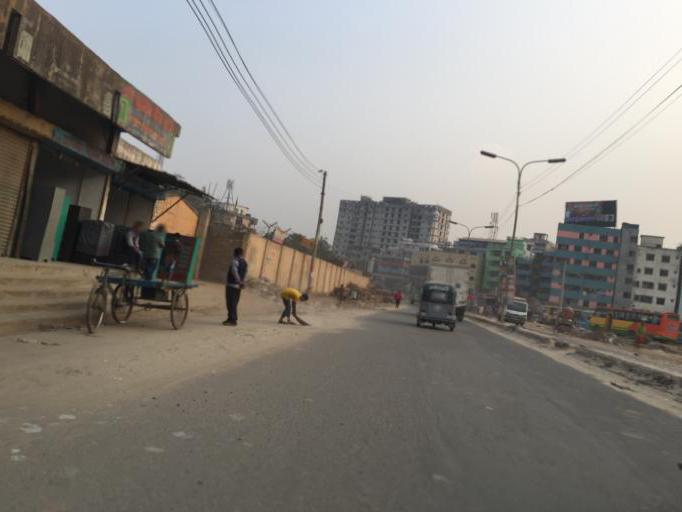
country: BD
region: Dhaka
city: Azimpur
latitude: 23.7968
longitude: 90.3473
